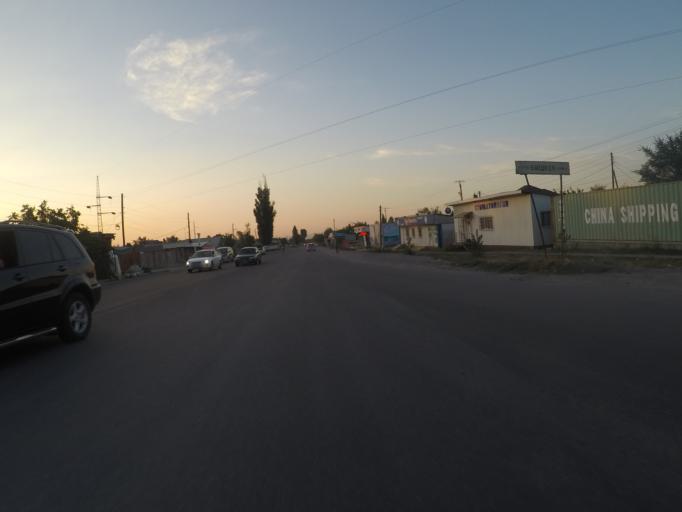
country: KG
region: Chuy
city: Lebedinovka
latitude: 42.8038
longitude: 74.6483
